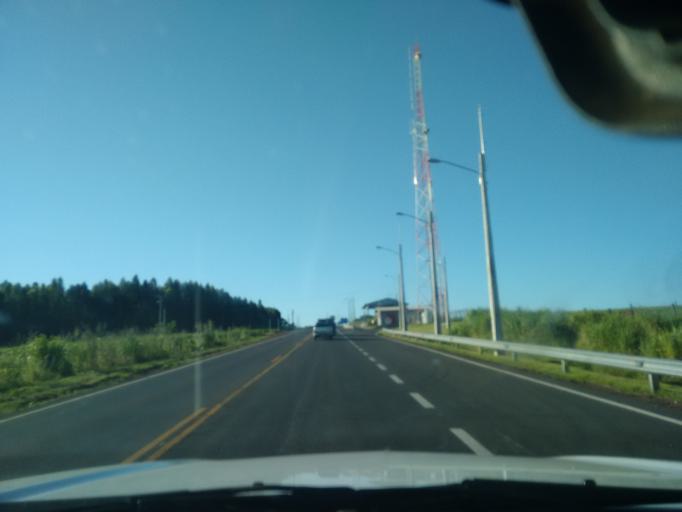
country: BR
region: Mato Grosso do Sul
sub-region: Eldorado
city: Eldorado
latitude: -23.8705
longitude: -54.3261
